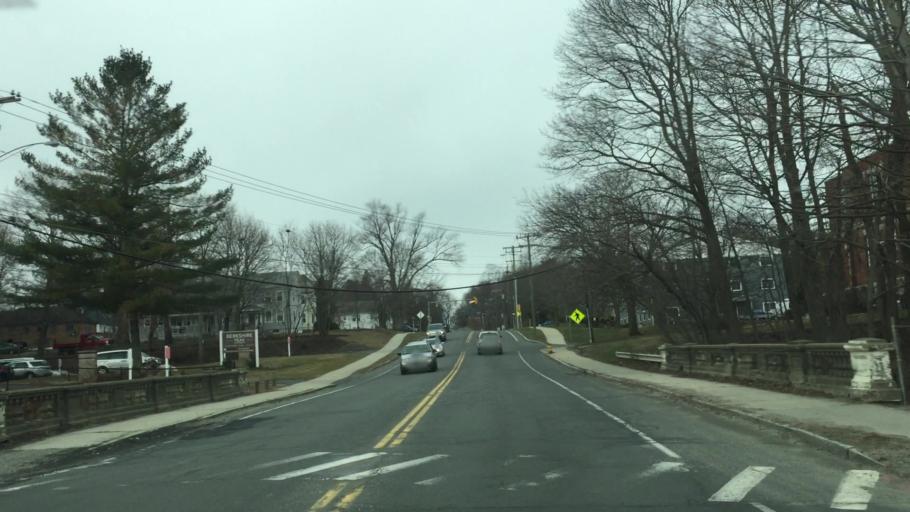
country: US
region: Massachusetts
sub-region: Berkshire County
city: Pittsfield
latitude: 42.4499
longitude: -73.2630
